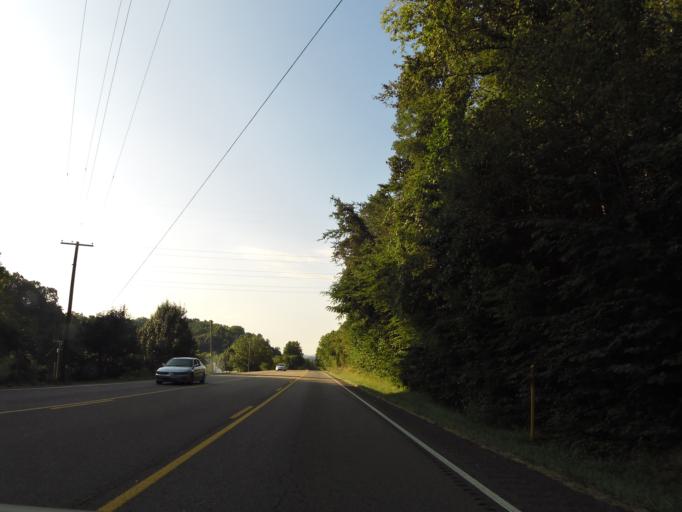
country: US
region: Tennessee
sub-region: Sevier County
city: Seymour
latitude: 35.9313
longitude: -83.8105
